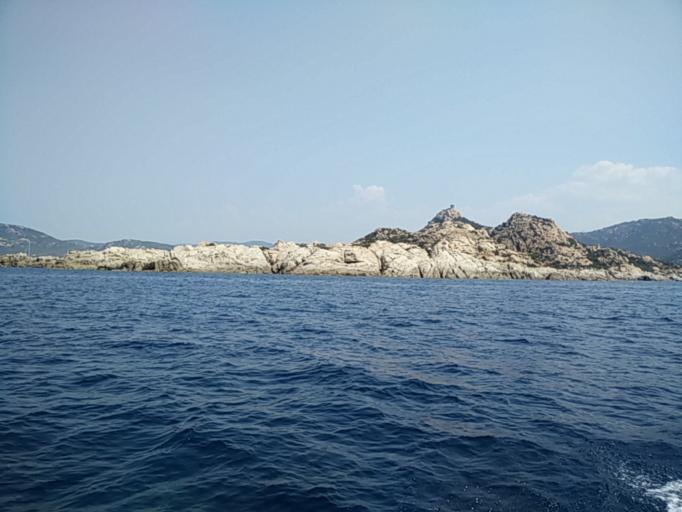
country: FR
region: Corsica
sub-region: Departement de la Corse-du-Sud
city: Sartene
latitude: 41.4875
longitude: 8.9199
